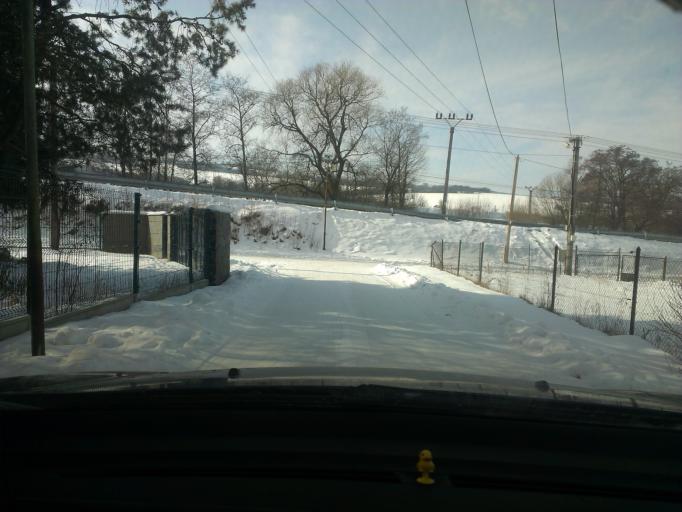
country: SK
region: Nitriansky
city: Handlova
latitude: 48.7842
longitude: 18.8420
